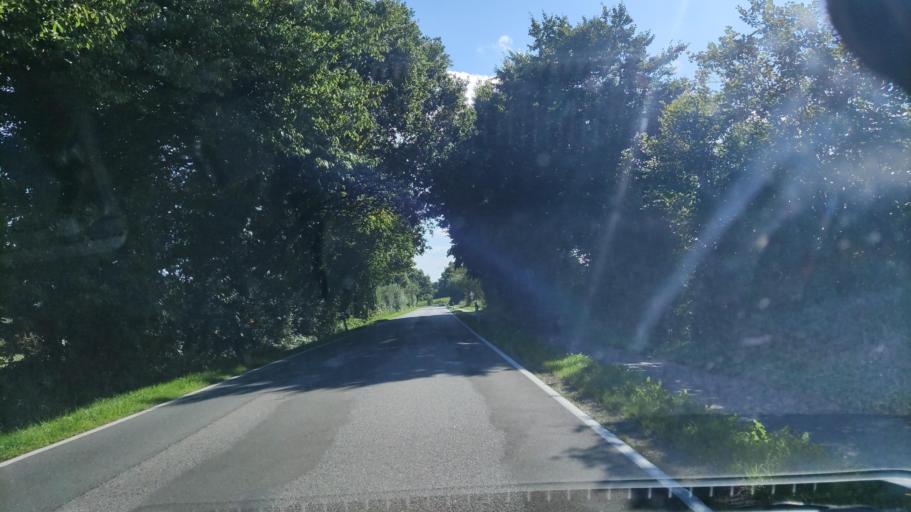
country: DE
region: Schleswig-Holstein
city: Oldenhutten
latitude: 54.1621
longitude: 9.7367
